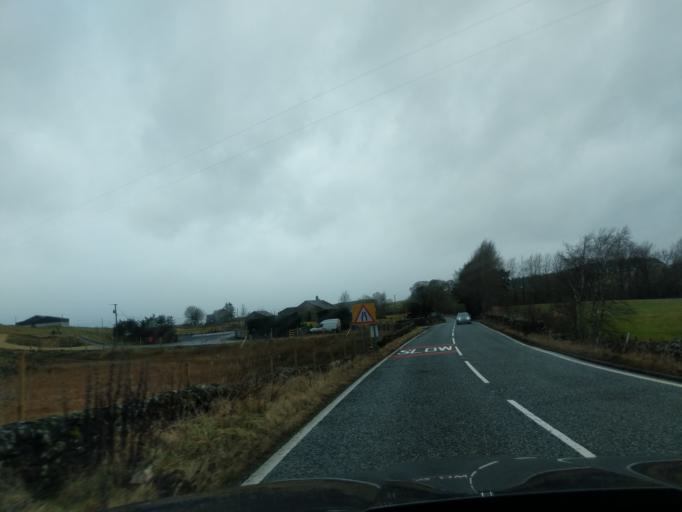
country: GB
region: England
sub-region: Northumberland
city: Otterburn
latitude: 55.2161
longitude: -2.1138
